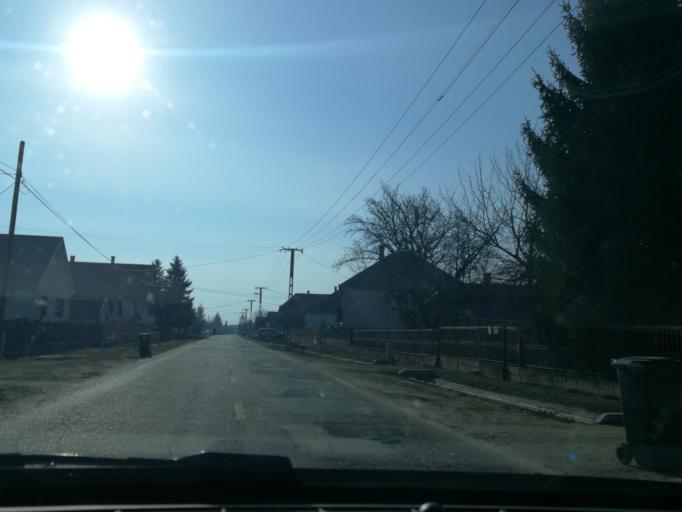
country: HU
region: Szabolcs-Szatmar-Bereg
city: Levelek
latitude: 47.9723
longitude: 21.9793
